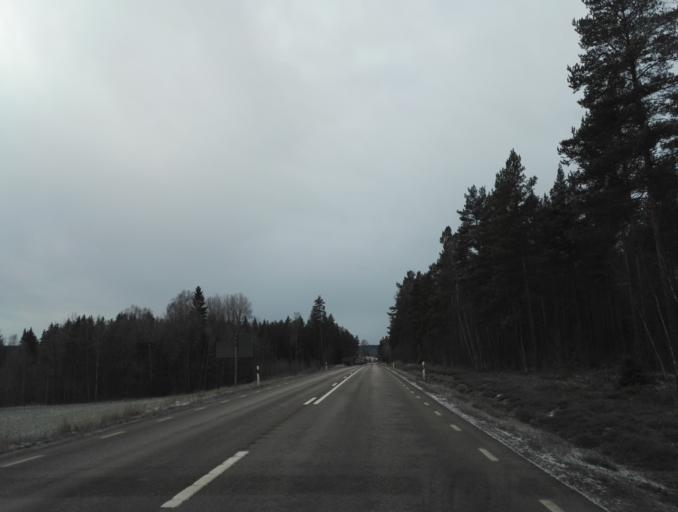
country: SE
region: Kalmar
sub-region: Hultsfreds Kommun
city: Virserum
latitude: 57.4200
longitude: 15.6296
